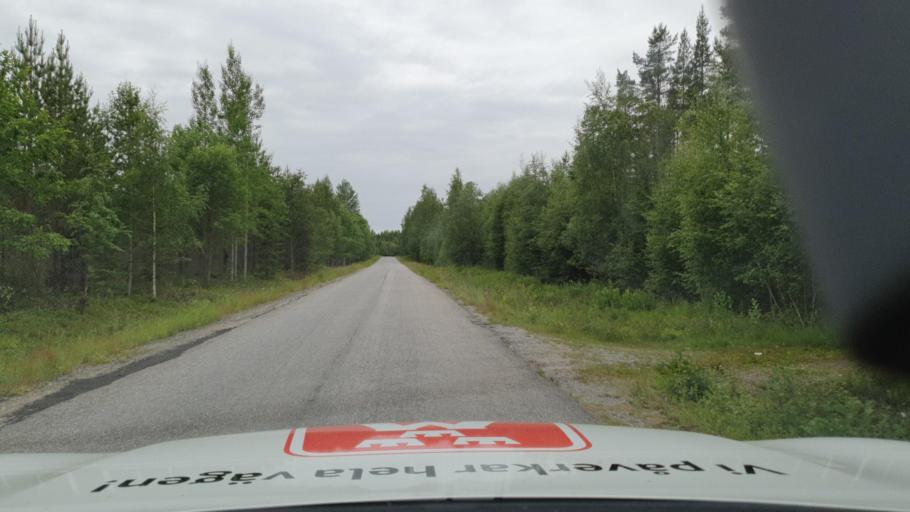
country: SE
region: Vaesterbotten
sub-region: Nordmalings Kommun
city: Nordmaling
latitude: 63.5308
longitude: 19.4303
